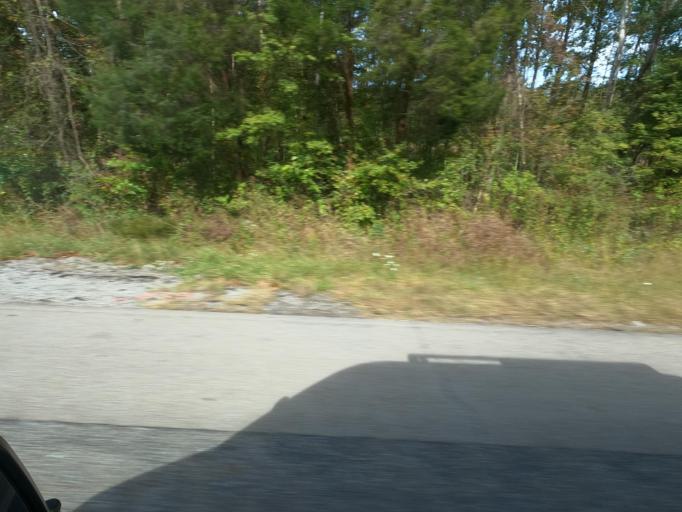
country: US
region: Tennessee
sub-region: Humphreys County
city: New Johnsonville
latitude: 35.8670
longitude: -87.8843
